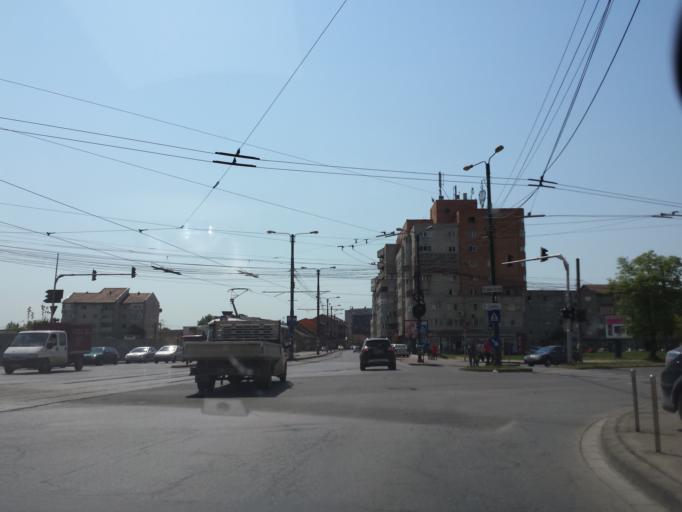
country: RO
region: Timis
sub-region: Comuna Dumbravita
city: Dumbravita
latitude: 45.7657
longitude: 21.2604
